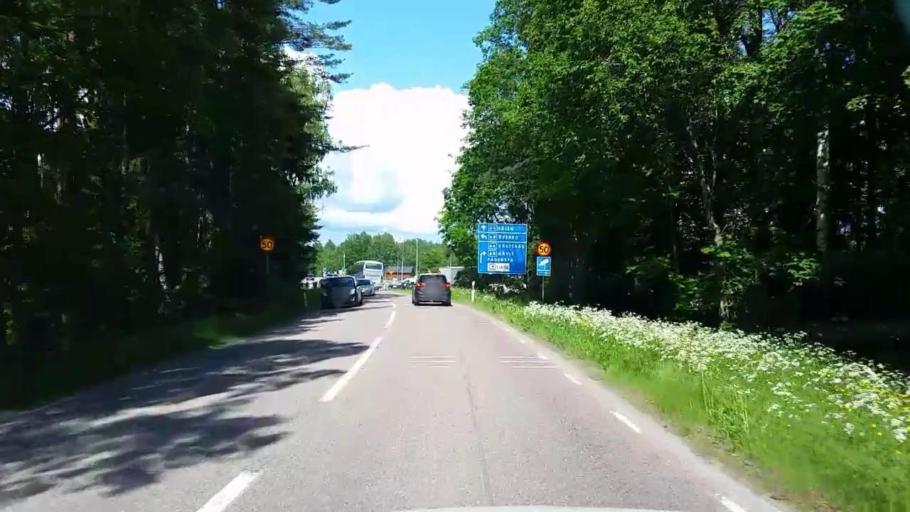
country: SE
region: Vaestmanland
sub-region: Fagersta Kommun
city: Fagersta
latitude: 59.9638
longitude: 15.7679
